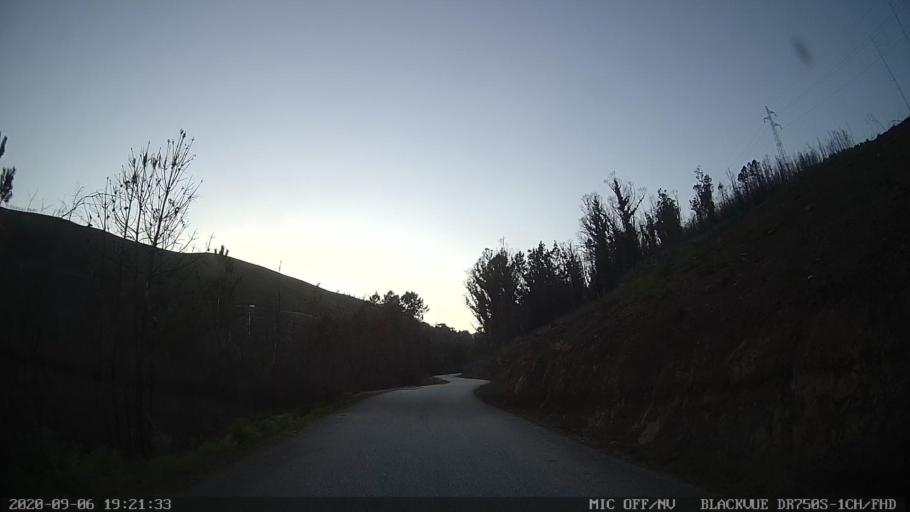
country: PT
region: Vila Real
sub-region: Mesao Frio
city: Mesao Frio
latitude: 41.1831
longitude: -7.9312
